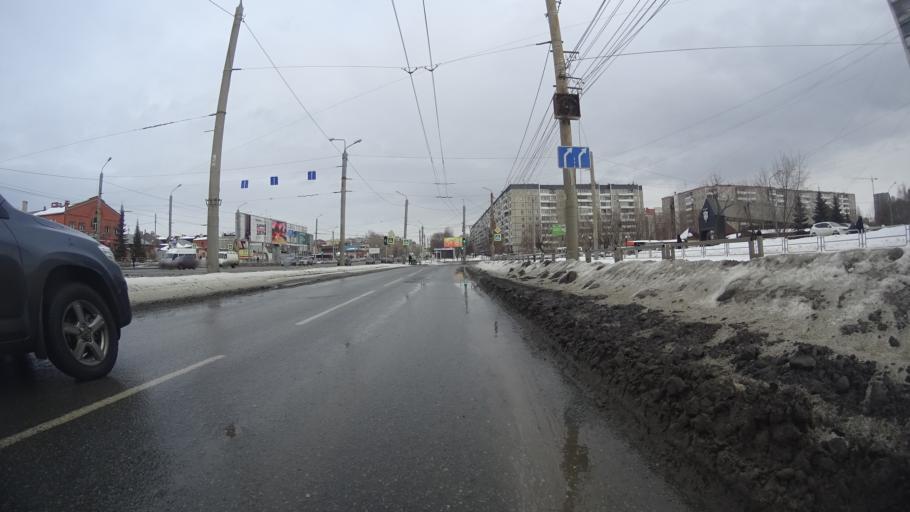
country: RU
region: Chelyabinsk
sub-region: Gorod Chelyabinsk
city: Chelyabinsk
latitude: 55.1781
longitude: 61.3567
